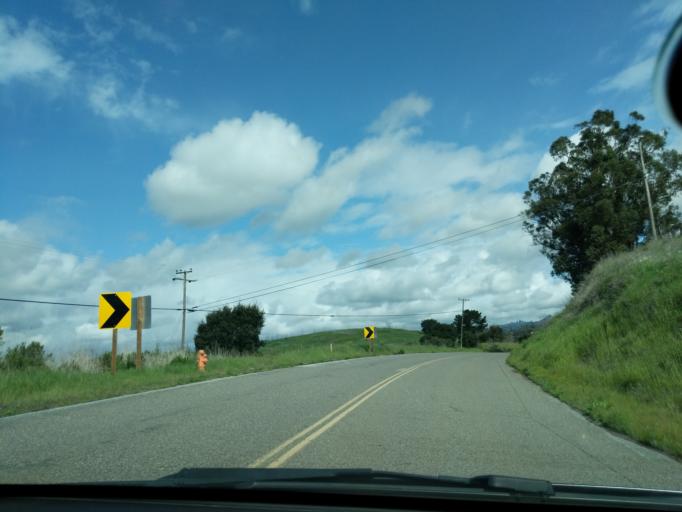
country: US
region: California
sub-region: San Benito County
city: Aromas
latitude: 36.8502
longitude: -121.6396
